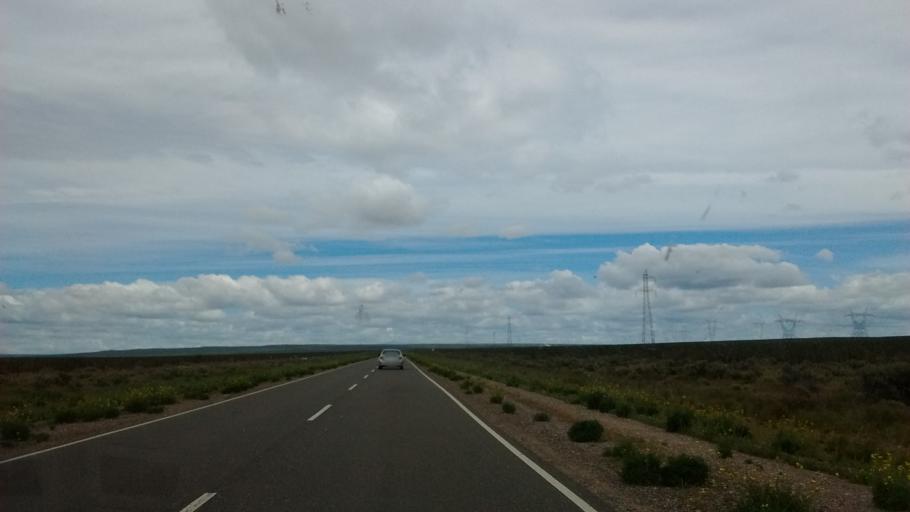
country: AR
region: Neuquen
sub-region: Departamento de Picun Leufu
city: Picun Leufu
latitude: -39.6956
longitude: -69.4862
